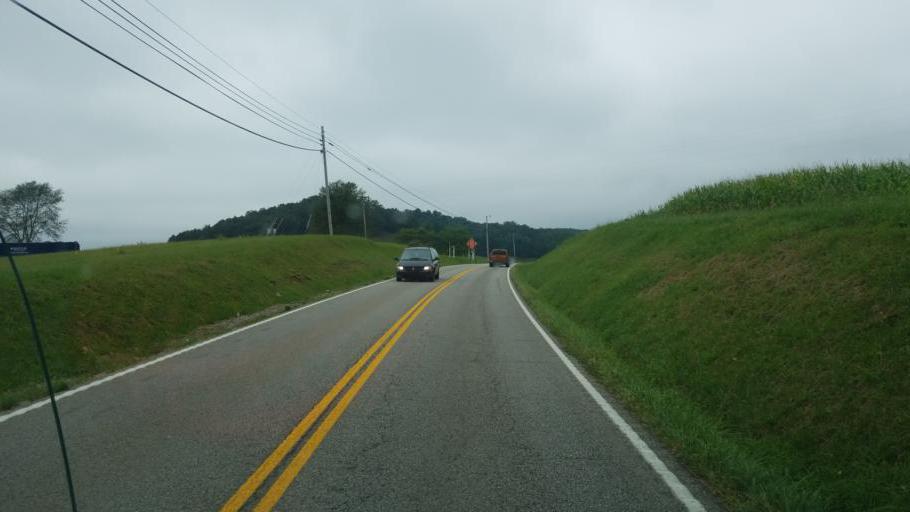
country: US
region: Kentucky
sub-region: Rowan County
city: Morehead
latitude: 38.2155
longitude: -83.4719
